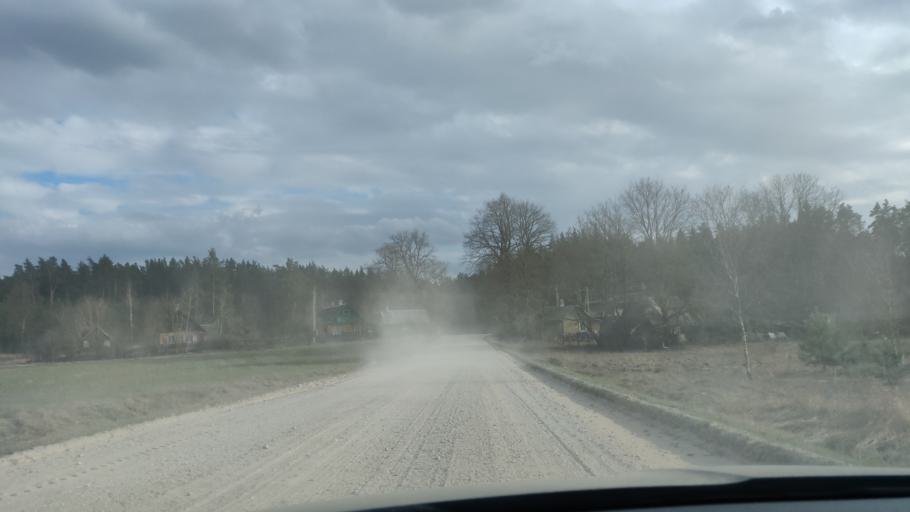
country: LT
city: Lentvaris
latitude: 54.6038
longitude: 25.0752
